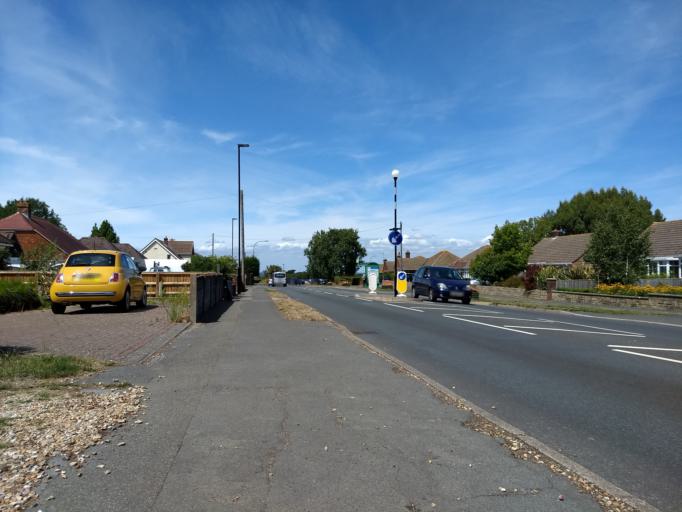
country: GB
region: England
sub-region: Isle of Wight
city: Northwood
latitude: 50.7441
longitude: -1.3120
